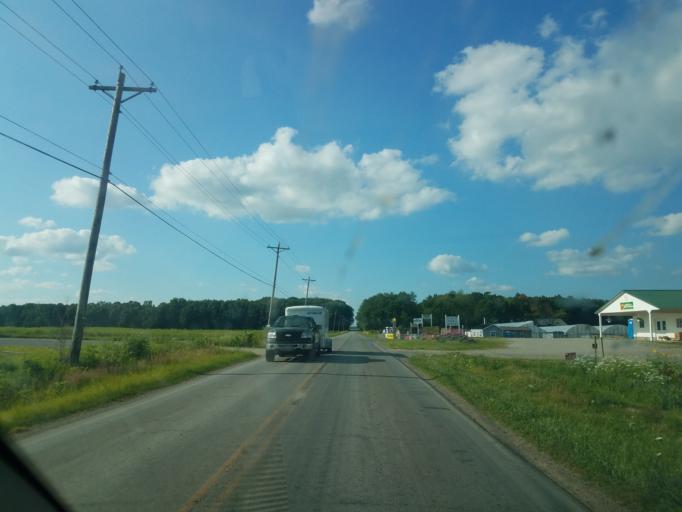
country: US
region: Ohio
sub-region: Wayne County
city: Apple Creek
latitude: 40.7362
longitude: -81.8962
